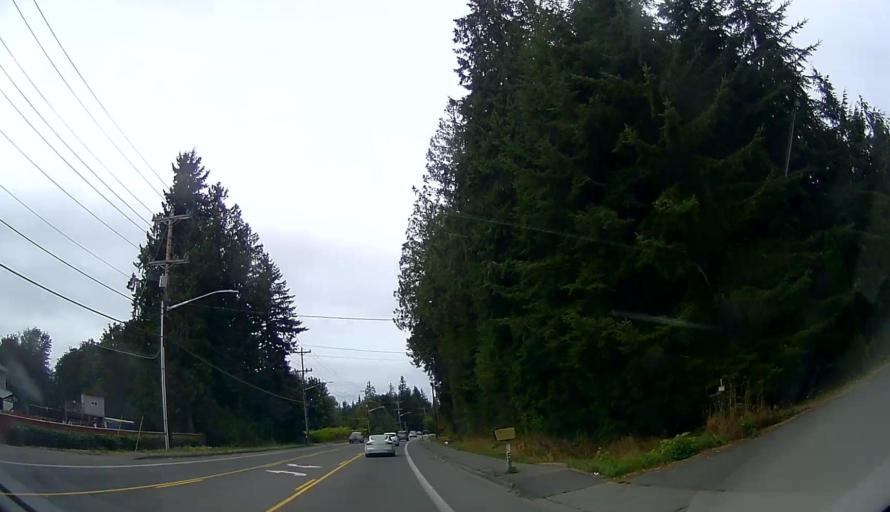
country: US
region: Washington
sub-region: Snohomish County
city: Marysville
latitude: 48.0406
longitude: -122.2258
